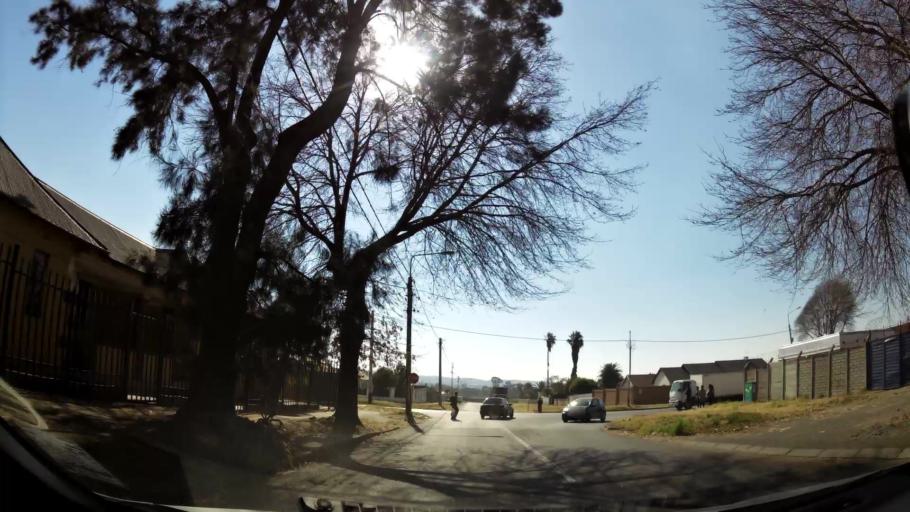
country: ZA
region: Gauteng
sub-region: City of Johannesburg Metropolitan Municipality
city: Johannesburg
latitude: -26.2396
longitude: 28.0737
